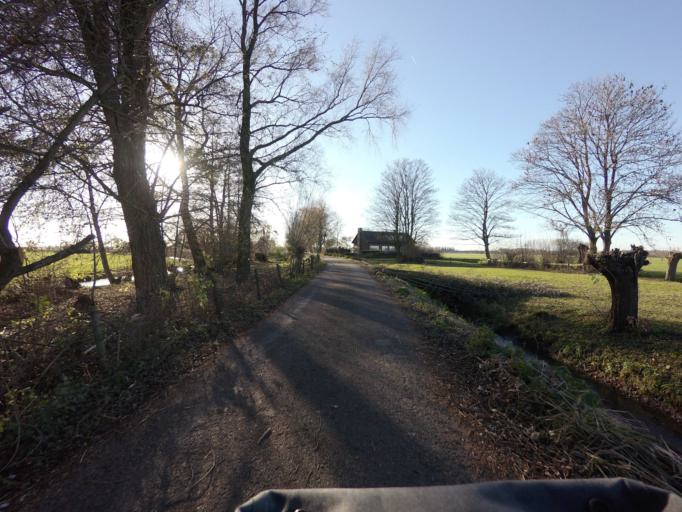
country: NL
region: North Holland
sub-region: Gemeente Amsterdam
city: Amsterdam-Zuidoost
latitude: 52.2546
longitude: 4.9794
